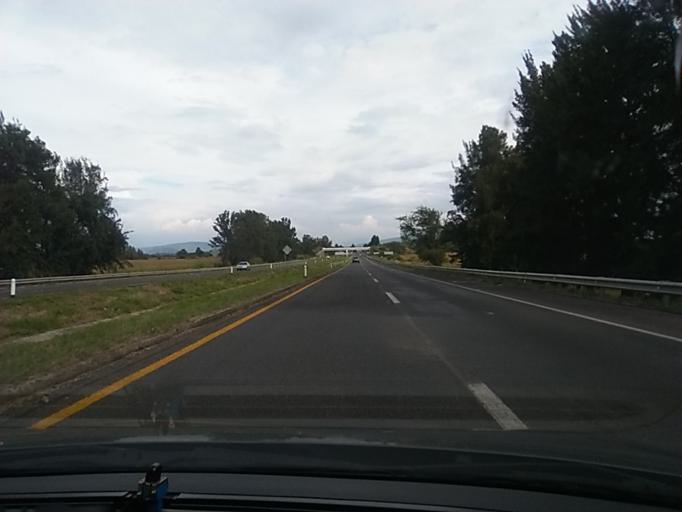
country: MX
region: Michoacan
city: Vistahermosa de Negrete
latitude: 20.2908
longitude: -102.4713
